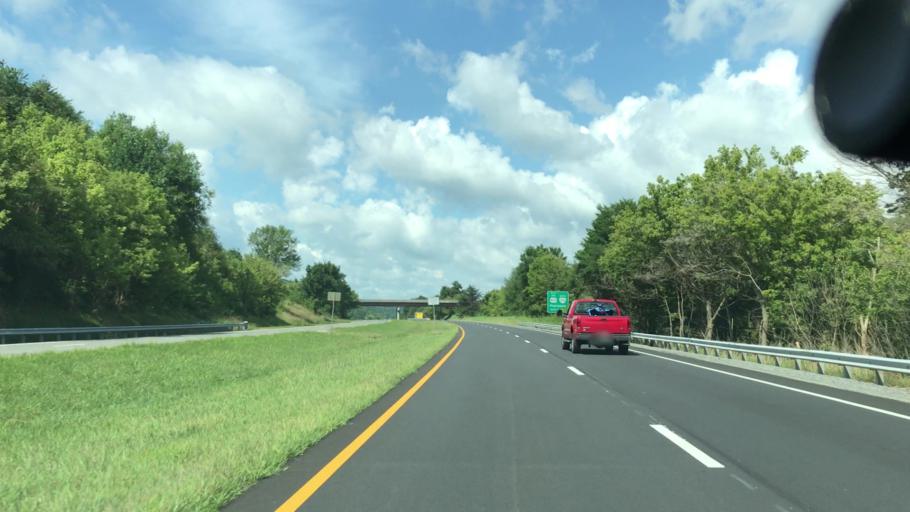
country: US
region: Virginia
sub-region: Giles County
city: Pearisburg
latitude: 37.3392
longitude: -80.7234
